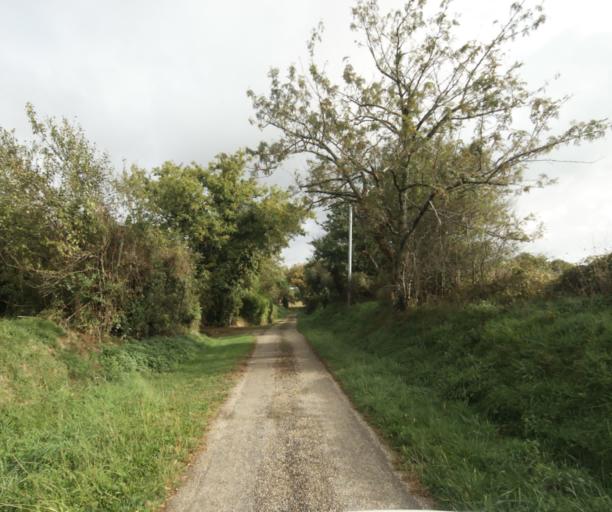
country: FR
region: Midi-Pyrenees
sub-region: Departement du Gers
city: Nogaro
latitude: 43.8230
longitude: -0.0750
